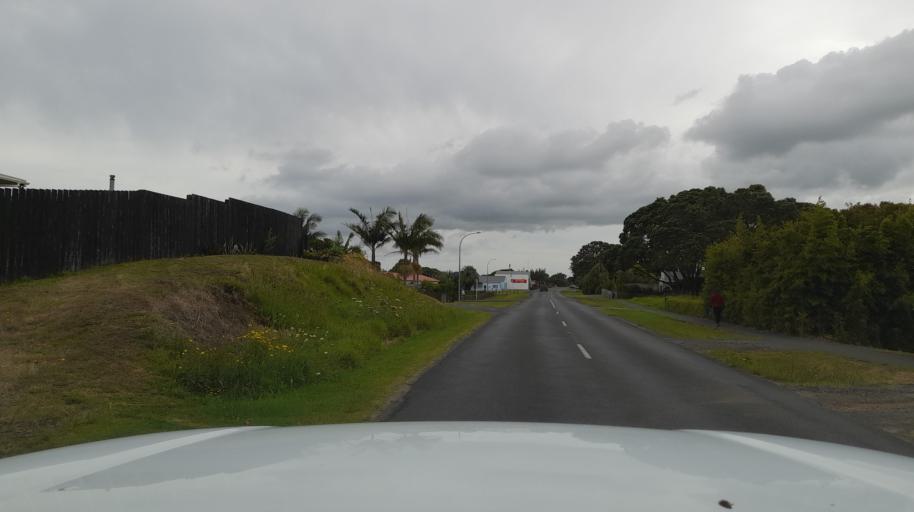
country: NZ
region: Northland
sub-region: Far North District
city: Ahipara
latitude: -35.1684
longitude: 173.1535
